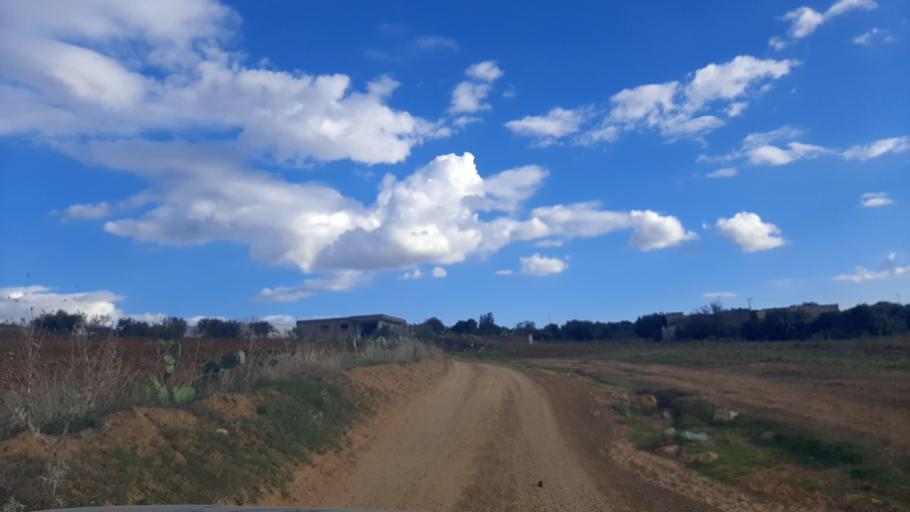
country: TN
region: Nabul
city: Bu `Urqub
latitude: 36.4441
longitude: 10.5054
